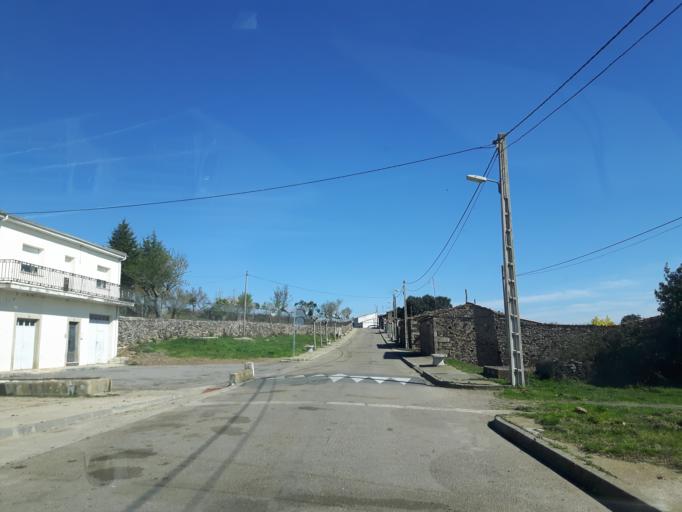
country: ES
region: Castille and Leon
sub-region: Provincia de Salamanca
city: Bermellar
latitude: 40.9979
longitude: -6.6670
